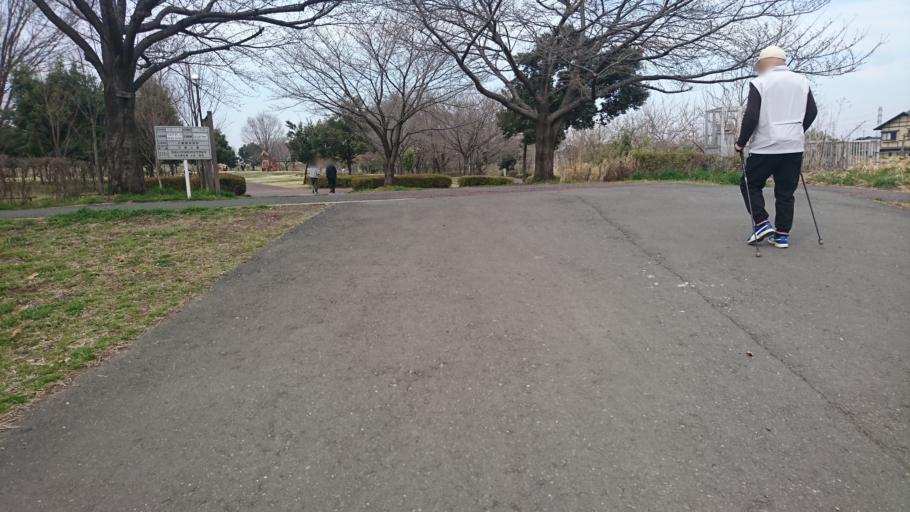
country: JP
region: Saitama
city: Kawagoe
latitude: 35.9155
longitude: 139.4531
